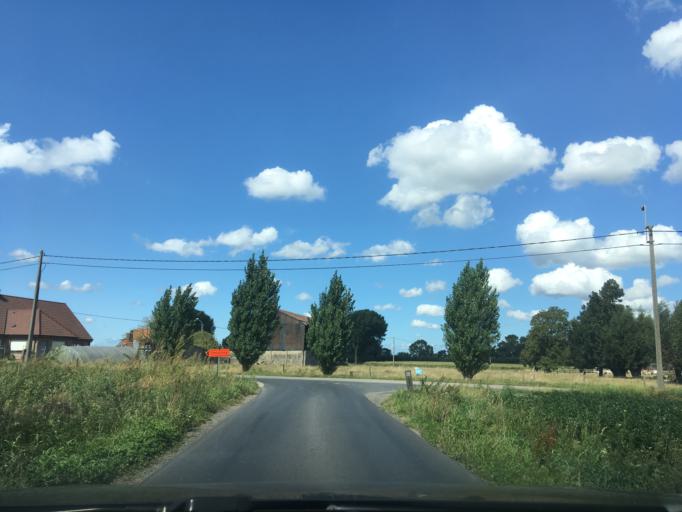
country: BE
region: Flanders
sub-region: Provincie West-Vlaanderen
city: Staden
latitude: 50.9826
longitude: 3.0313
